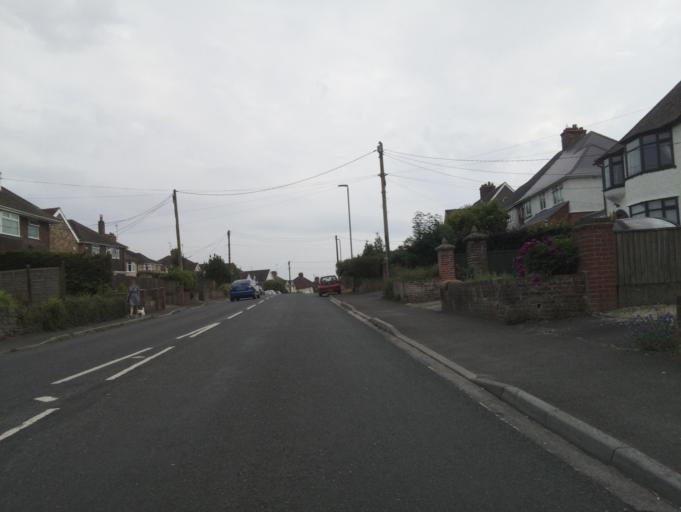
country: GB
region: England
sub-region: Somerset
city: Yeovil
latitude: 50.9562
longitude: -2.6341
